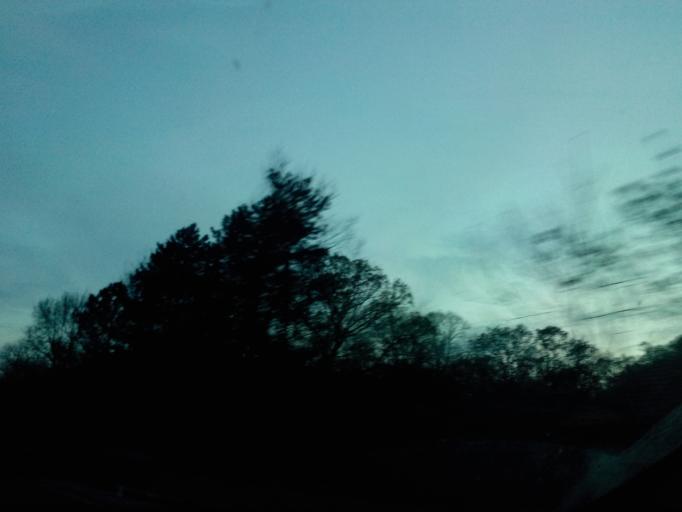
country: RO
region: Ilfov
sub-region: Comuna Ciolpani
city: Ciolpani
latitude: 44.7002
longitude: 26.0871
